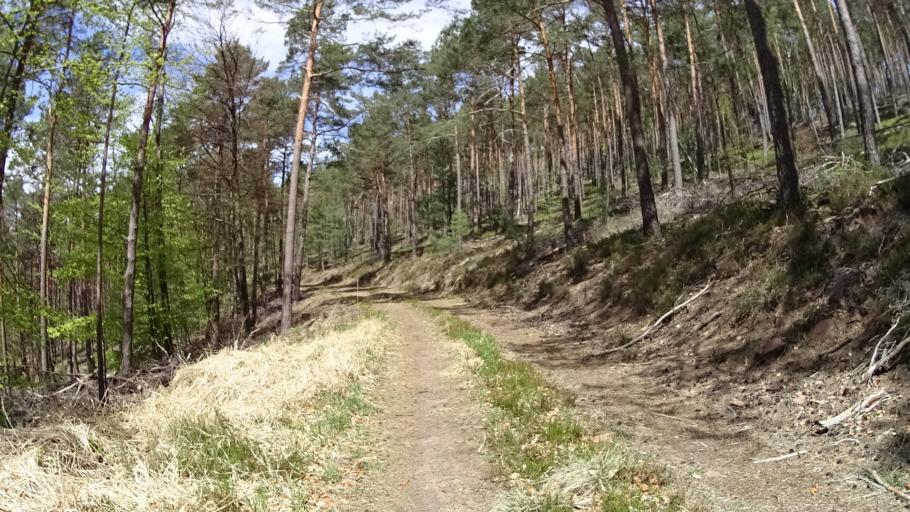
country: DE
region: Rheinland-Pfalz
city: Ramberg
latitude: 49.3087
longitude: 8.0050
